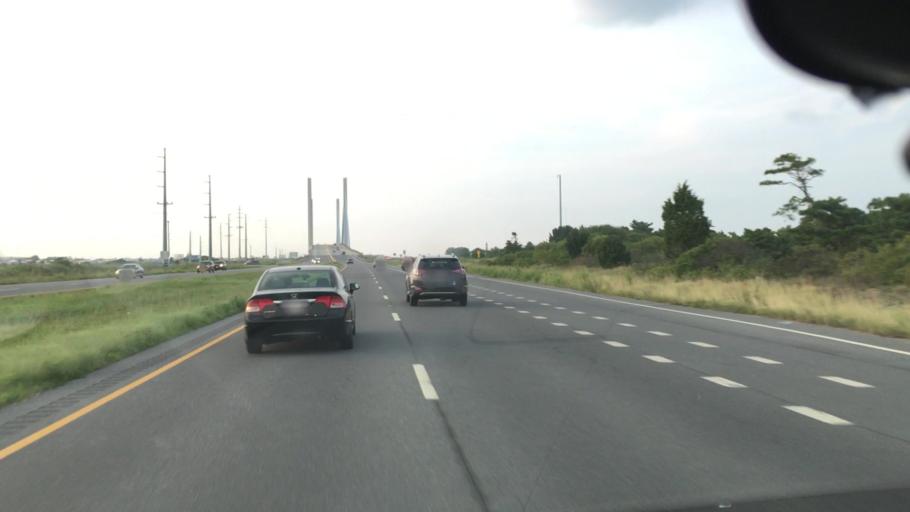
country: US
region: Delaware
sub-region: Sussex County
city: Bethany Beach
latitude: 38.5995
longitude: -75.0621
